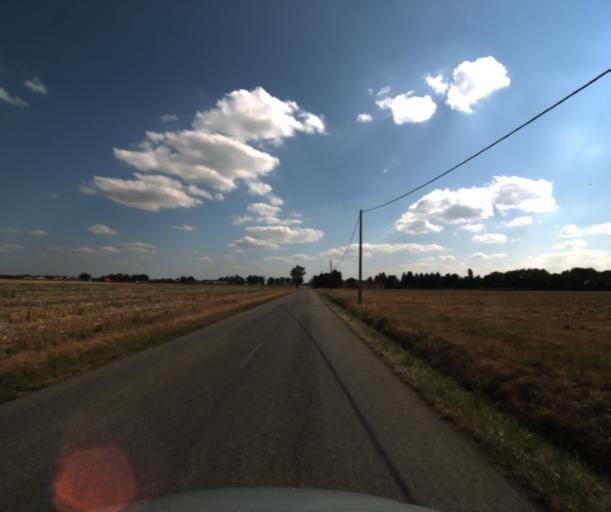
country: FR
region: Midi-Pyrenees
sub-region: Departement de la Haute-Garonne
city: Fontenilles
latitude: 43.5329
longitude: 1.1846
